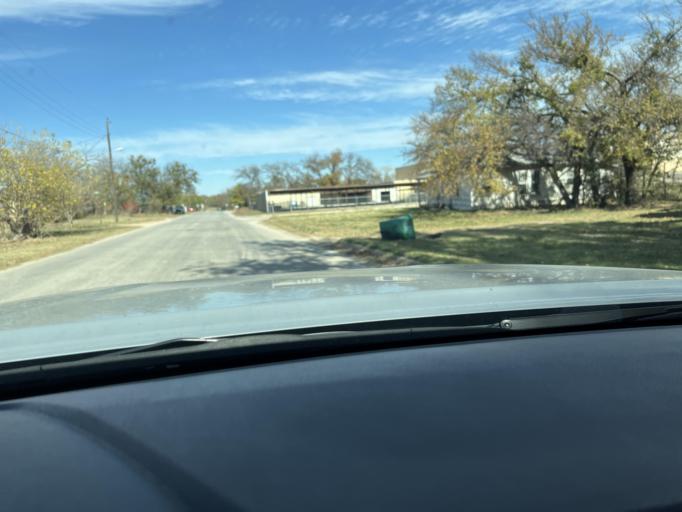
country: US
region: Texas
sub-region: Eastland County
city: Eastland
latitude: 32.3977
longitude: -98.8307
